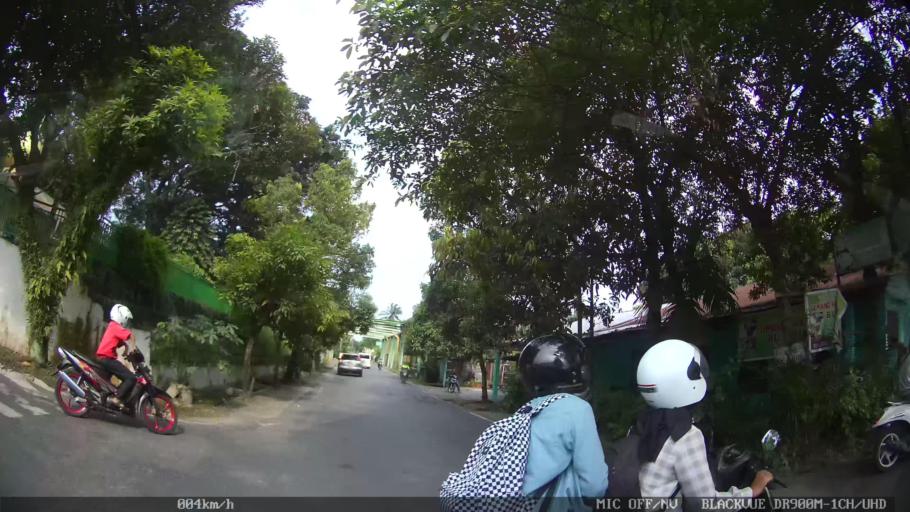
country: ID
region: North Sumatra
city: Medan
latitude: 3.5570
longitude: 98.6827
